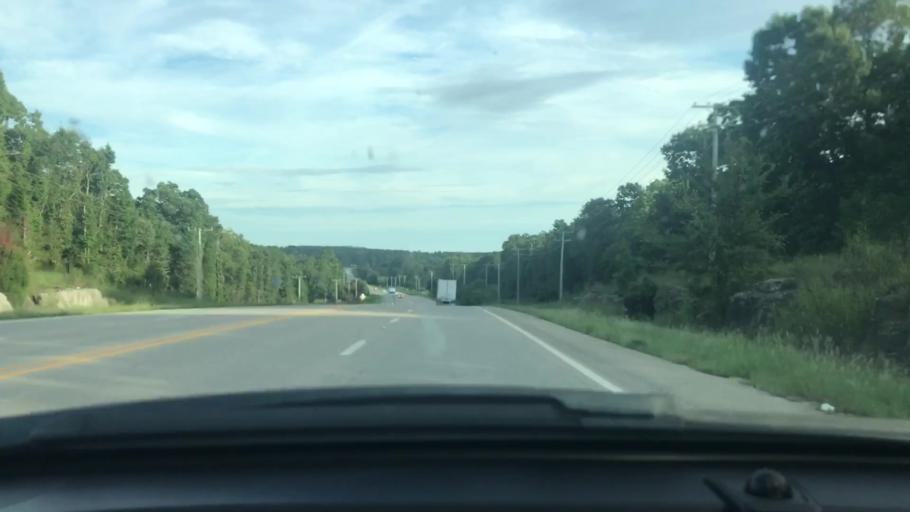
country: US
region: Arkansas
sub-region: Lawrence County
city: Hoxie
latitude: 36.1271
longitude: -91.1561
